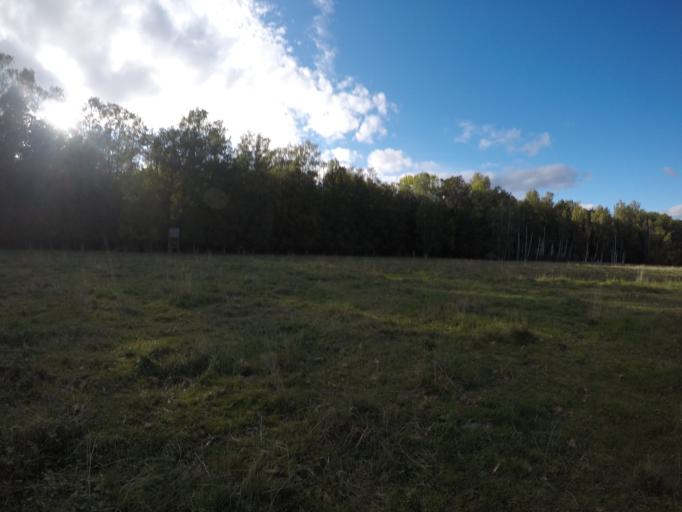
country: SE
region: Soedermanland
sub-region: Eskilstuna Kommun
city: Kvicksund
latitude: 59.4807
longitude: 16.2431
